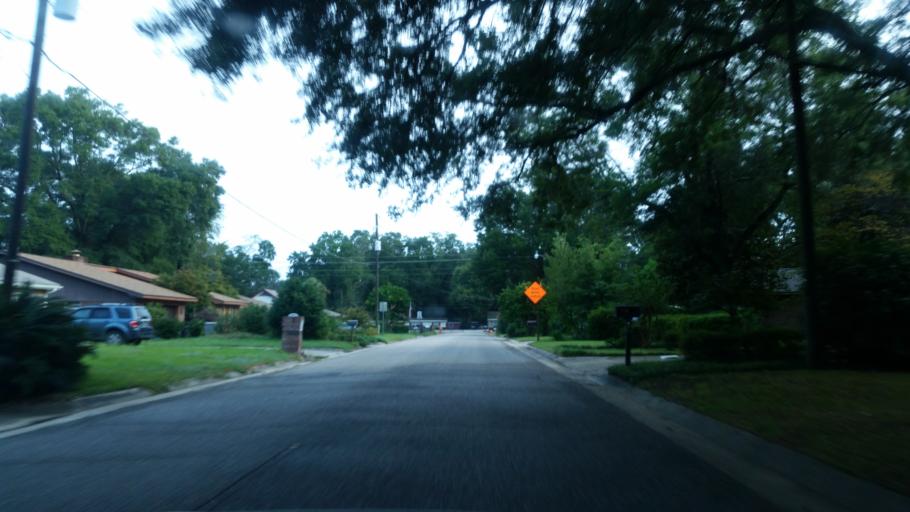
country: US
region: Florida
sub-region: Escambia County
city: Ferry Pass
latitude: 30.5088
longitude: -87.2028
